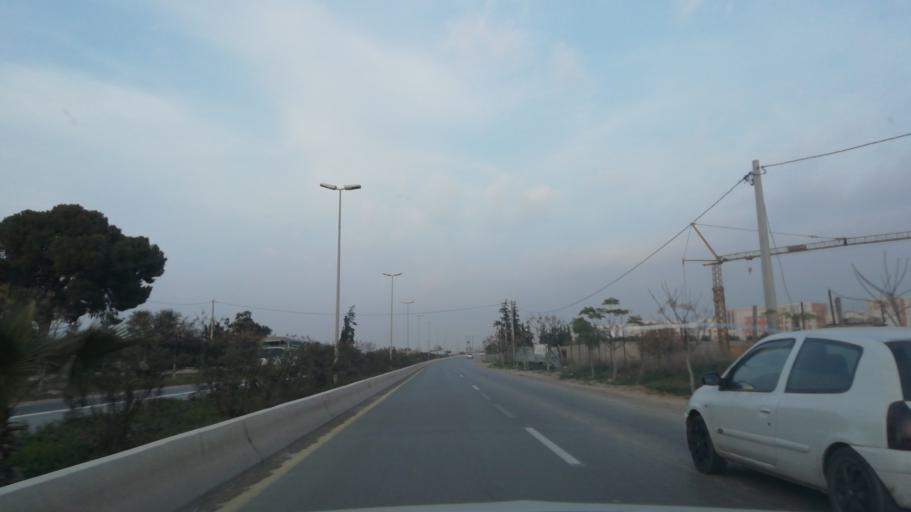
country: DZ
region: Sidi Bel Abbes
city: Sidi Bel Abbes
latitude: 35.2153
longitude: -0.6526
